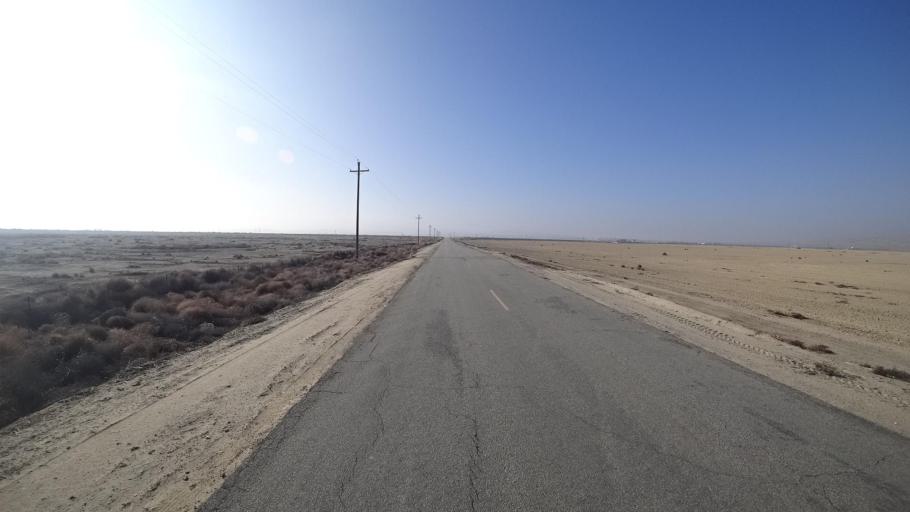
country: US
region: California
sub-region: Kern County
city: Maricopa
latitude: 35.1012
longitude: -119.3605
